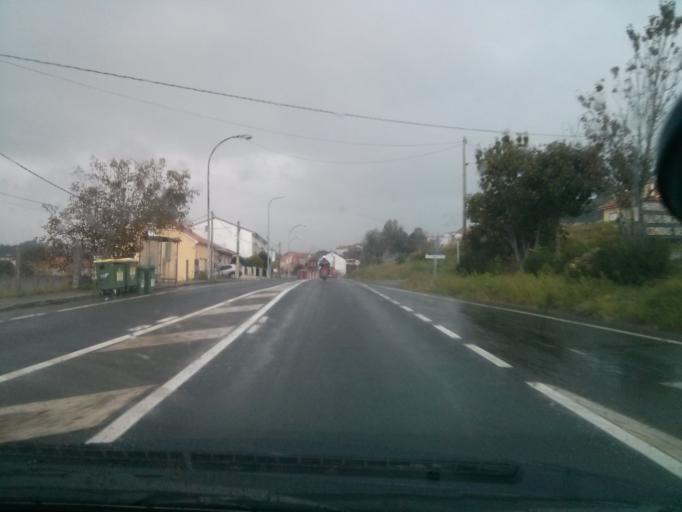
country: ES
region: Galicia
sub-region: Provincia da Coruna
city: Noia
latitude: 42.8044
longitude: -8.8843
